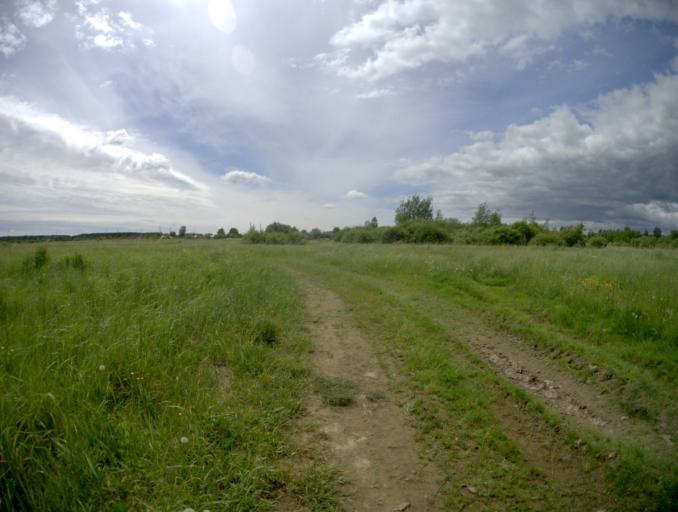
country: RU
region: Ivanovo
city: Savino
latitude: 56.5931
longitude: 41.2306
